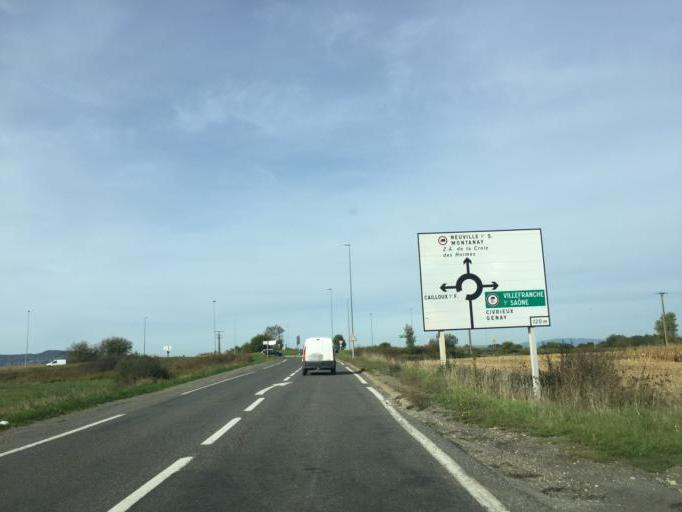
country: FR
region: Rhone-Alpes
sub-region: Departement du Rhone
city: Montanay
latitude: 45.8826
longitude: 4.8856
